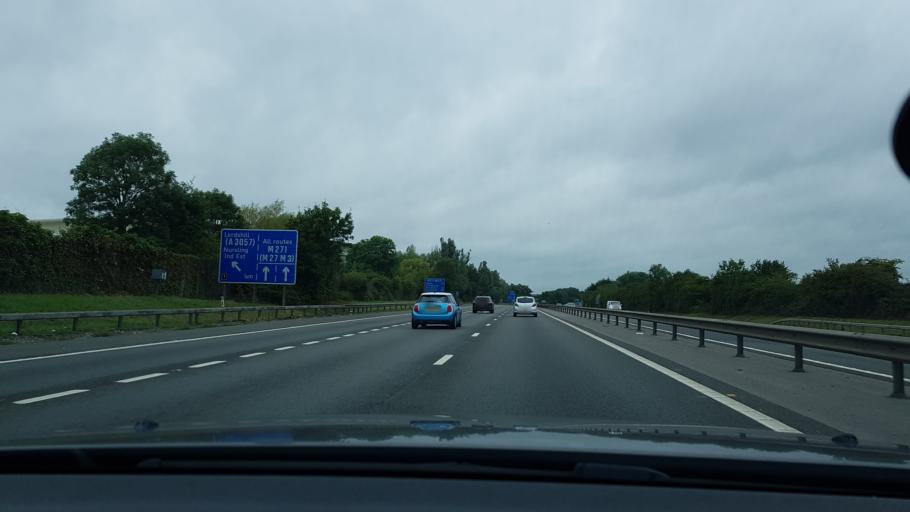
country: GB
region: England
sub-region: Hampshire
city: Totton
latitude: 50.9251
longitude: -1.4708
